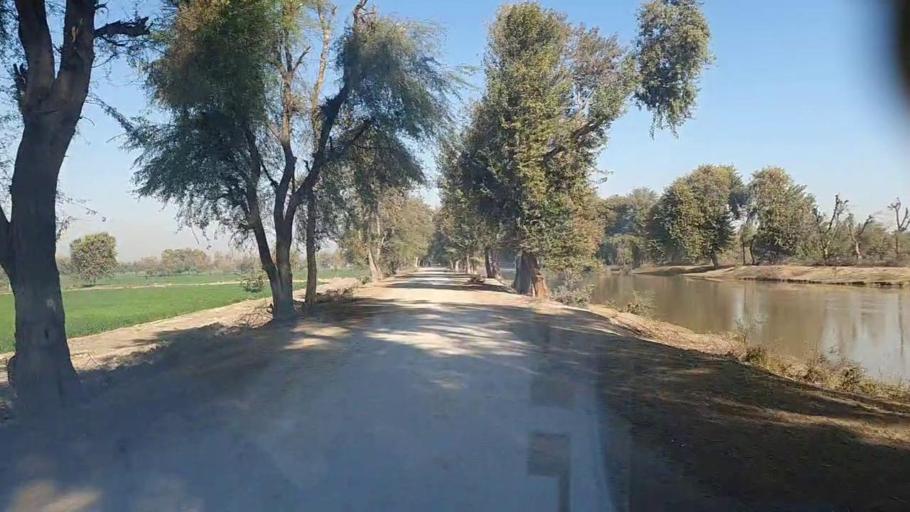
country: PK
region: Sindh
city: Khairpur
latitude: 27.9971
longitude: 69.6526
